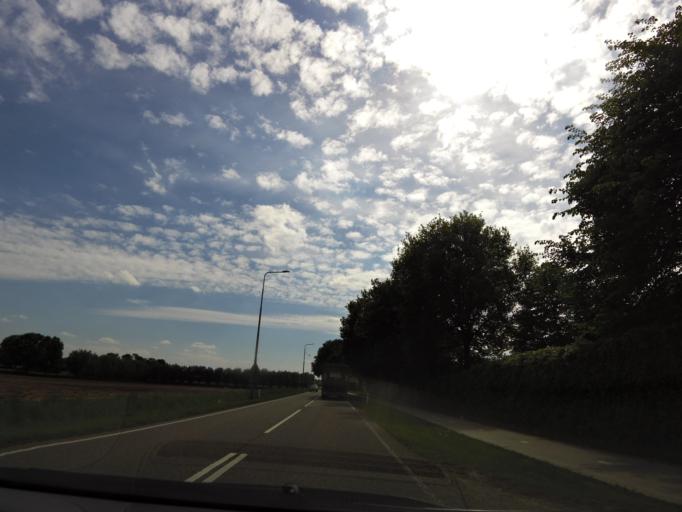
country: NL
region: Limburg
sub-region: Gemeente Leudal
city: Haelen
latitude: 51.3043
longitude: 5.9698
